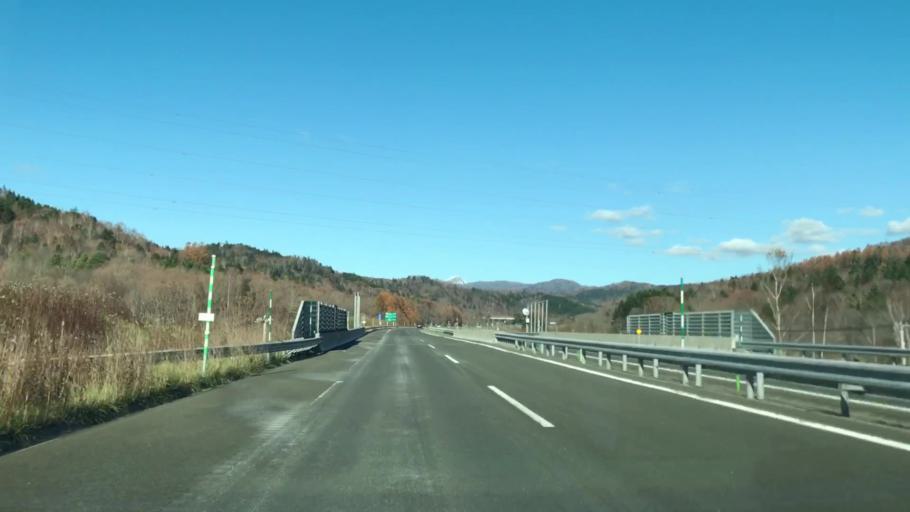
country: JP
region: Hokkaido
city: Shimo-furano
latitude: 42.9278
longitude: 142.2038
